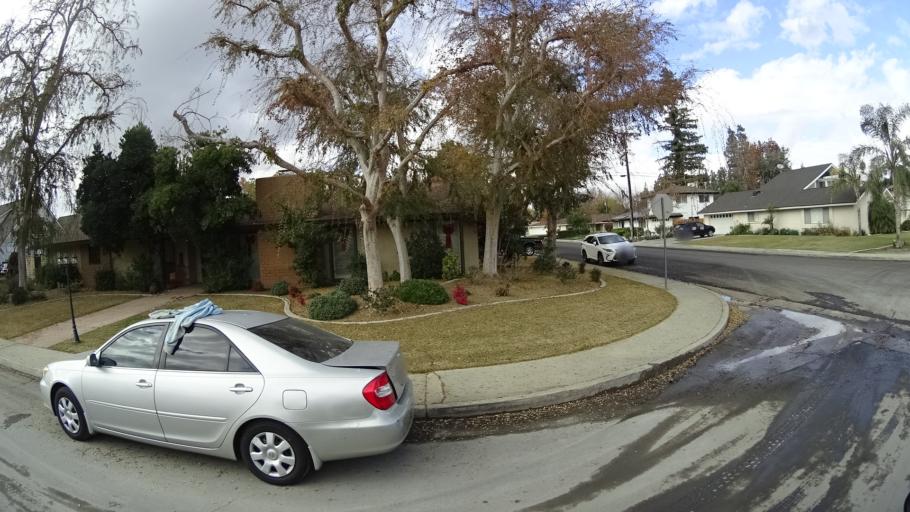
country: US
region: California
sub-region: Kern County
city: Greenacres
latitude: 35.3483
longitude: -119.0833
